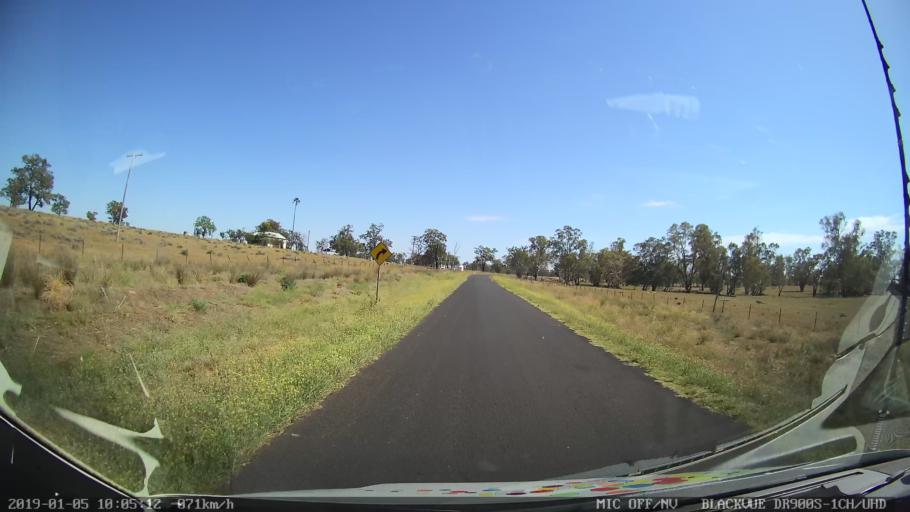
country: AU
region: New South Wales
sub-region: Gilgandra
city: Gilgandra
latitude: -31.6686
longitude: 148.8647
